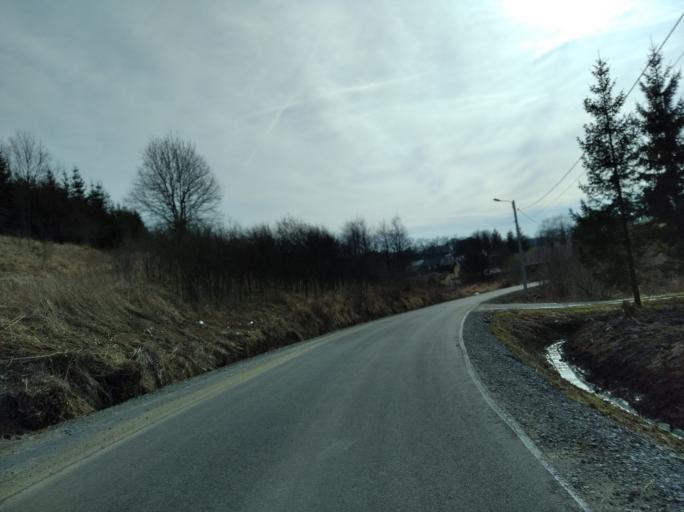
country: PL
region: Subcarpathian Voivodeship
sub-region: Powiat brzozowski
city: Jasienica Rosielna
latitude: 49.7603
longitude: 21.9477
